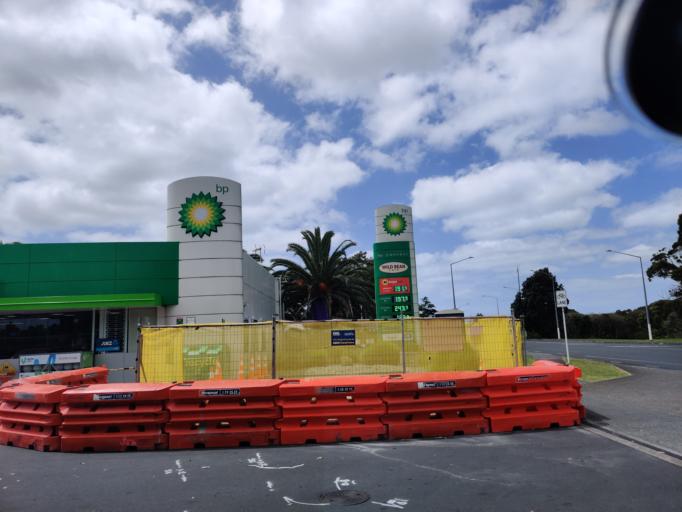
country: NZ
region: Auckland
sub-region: Auckland
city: Mangere
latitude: -36.9537
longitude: 174.7910
